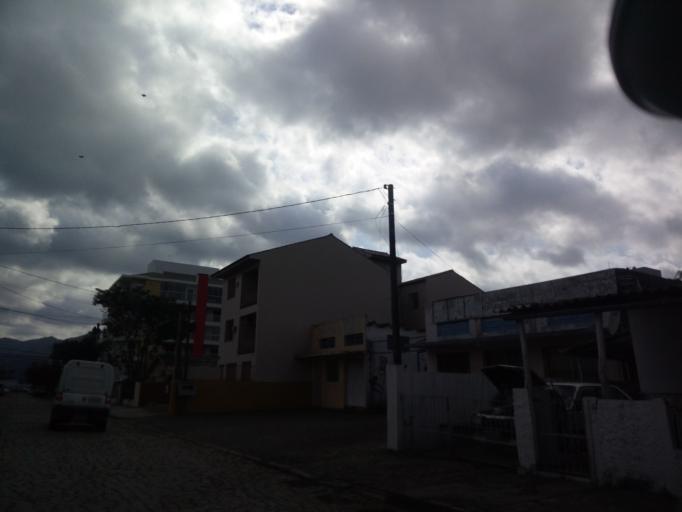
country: BR
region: Rio Grande do Sul
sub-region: Santa Maria
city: Santa Maria
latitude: -29.7035
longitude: -53.7246
